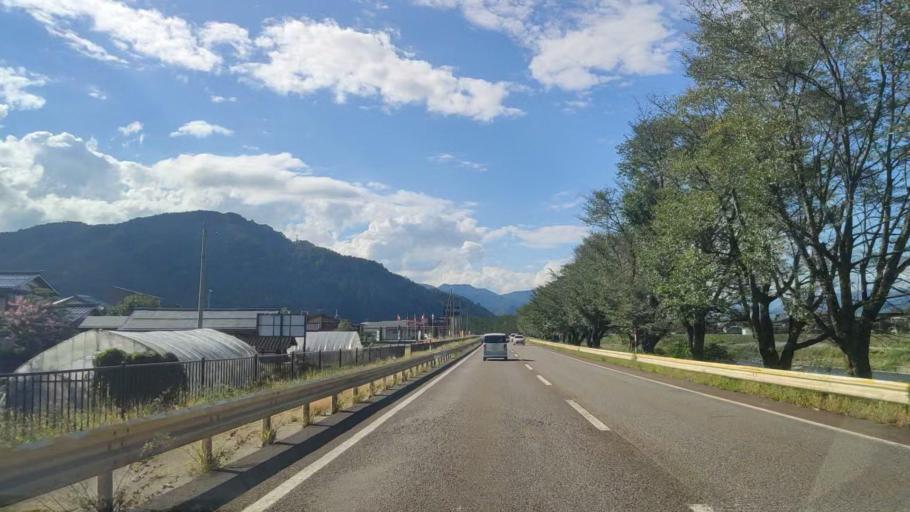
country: JP
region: Gifu
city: Takayama
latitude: 36.2074
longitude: 137.2178
